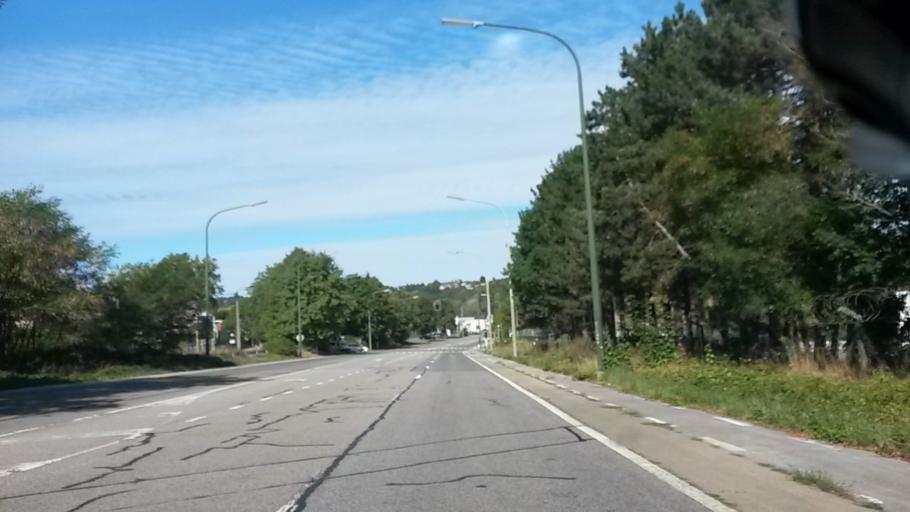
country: BE
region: Wallonia
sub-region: Province de Liege
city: Huy
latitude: 50.5312
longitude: 5.2682
